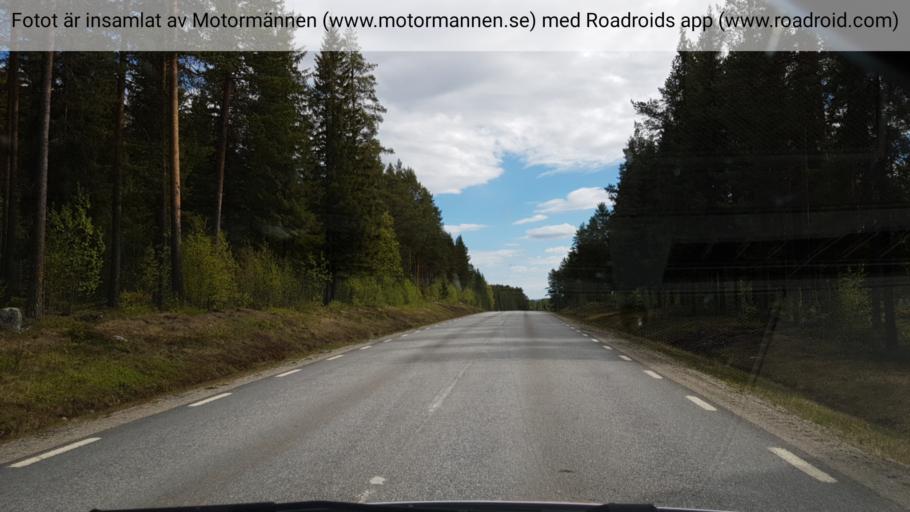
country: SE
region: Vaesterbotten
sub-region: Bjurholms Kommun
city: Bjurholm
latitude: 64.2690
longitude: 19.2681
